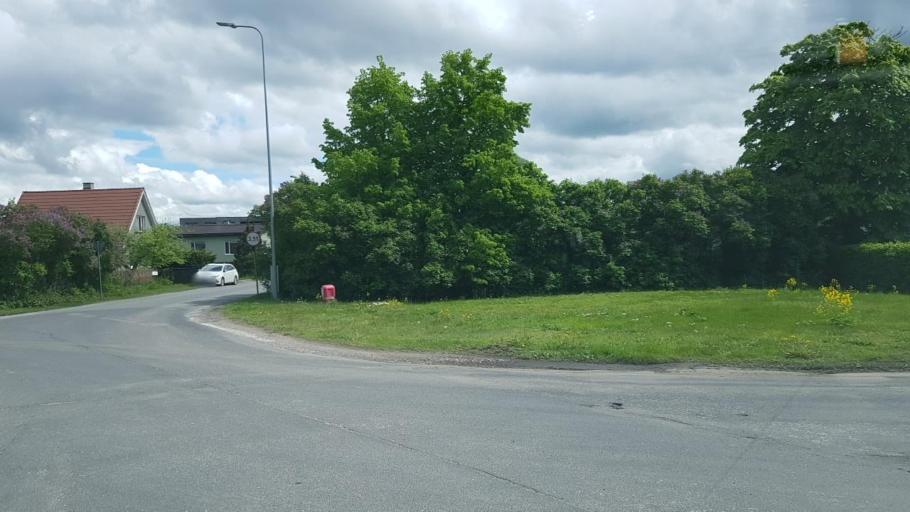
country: EE
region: Laeaene
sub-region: Haapsalu linn
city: Haapsalu
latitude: 58.9281
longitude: 23.5385
